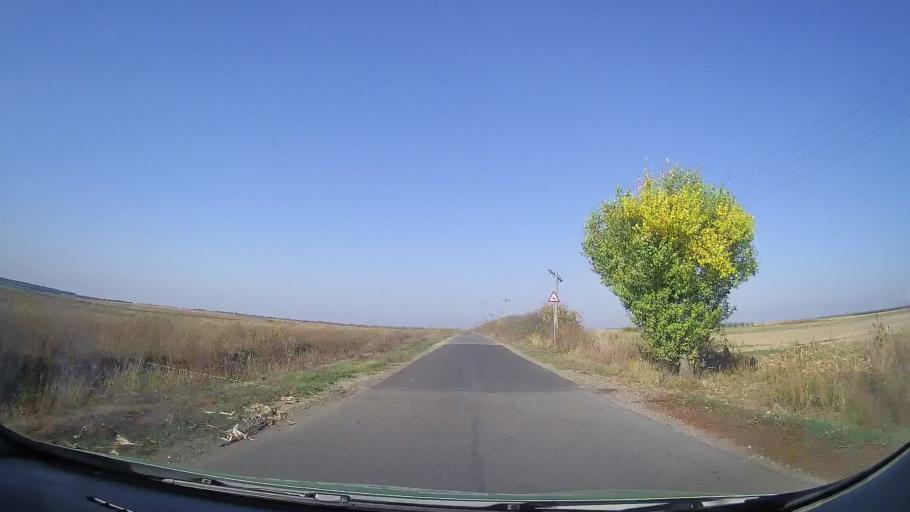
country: RO
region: Satu Mare
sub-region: Oras Tasnad
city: Tasnad
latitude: 47.4777
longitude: 22.5525
